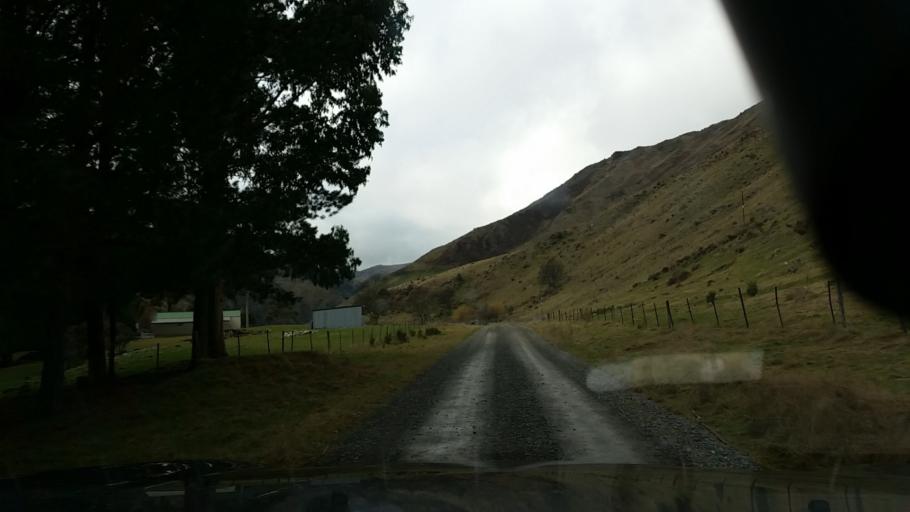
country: NZ
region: Tasman
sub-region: Tasman District
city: Brightwater
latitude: -41.7358
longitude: 173.4228
